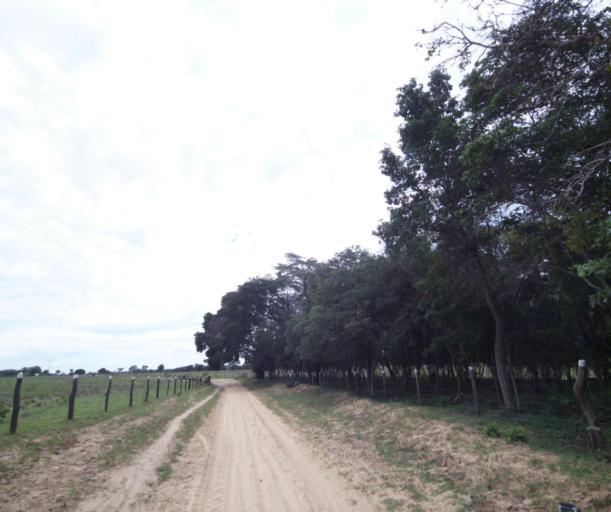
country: BR
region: Bahia
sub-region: Carinhanha
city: Carinhanha
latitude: -14.2550
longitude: -44.3591
